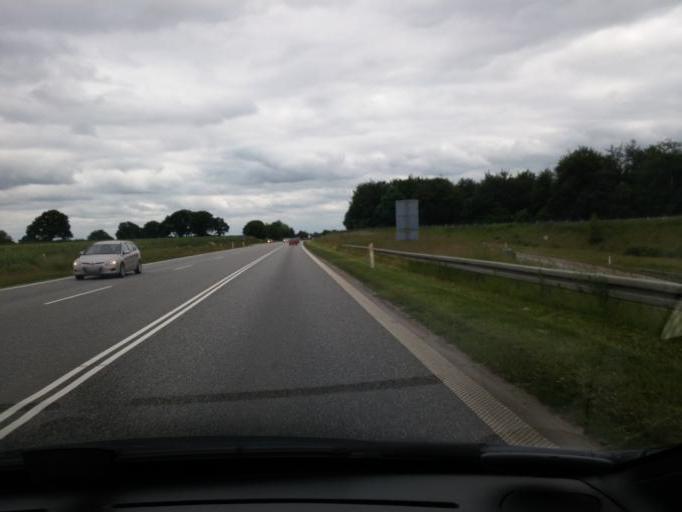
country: DK
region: Capital Region
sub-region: Hillerod Kommune
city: Hillerod
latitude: 55.9192
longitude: 12.2611
